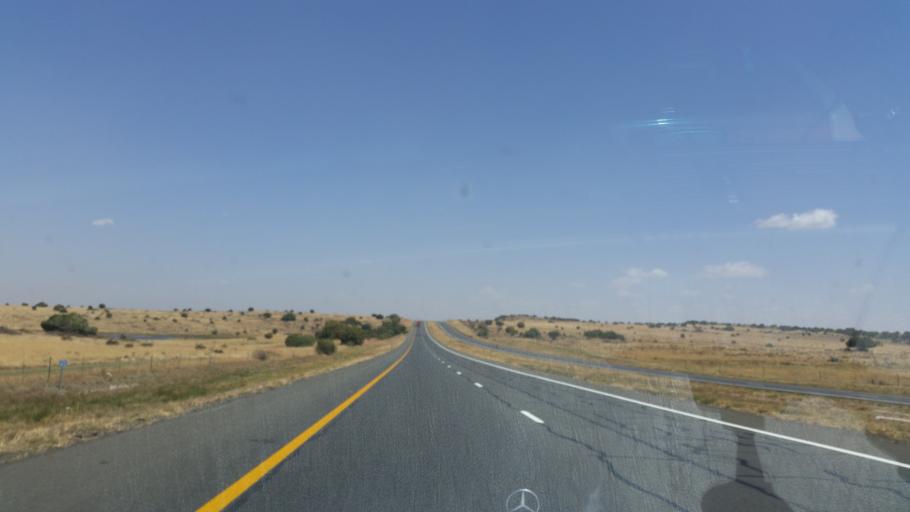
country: ZA
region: Orange Free State
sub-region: Lejweleputswa District Municipality
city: Brandfort
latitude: -28.9119
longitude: 26.4546
